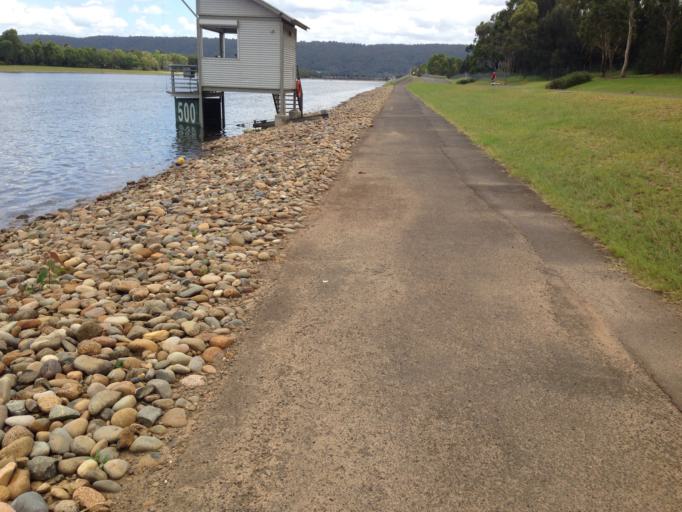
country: AU
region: New South Wales
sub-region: Penrith Municipality
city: Penrith
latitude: -33.7243
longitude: 150.6874
